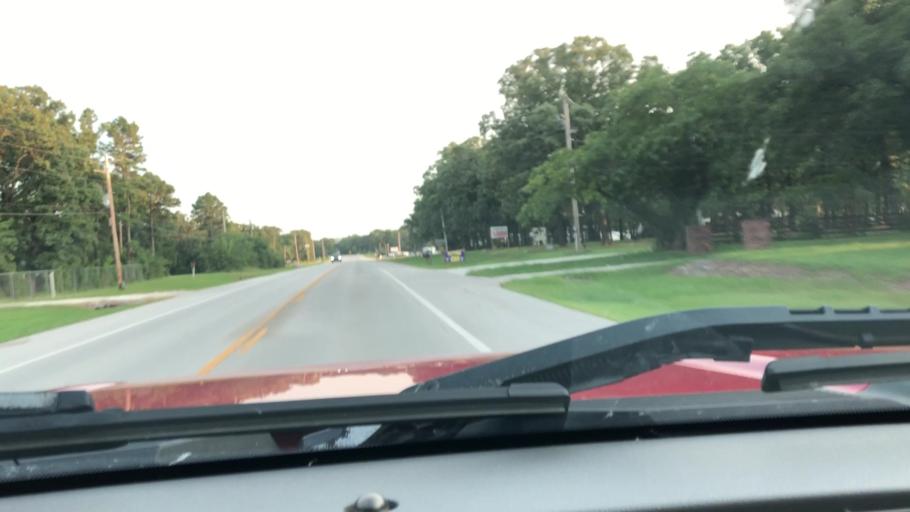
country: US
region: Missouri
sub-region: Jasper County
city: Duquesne
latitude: 36.9858
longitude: -94.4637
